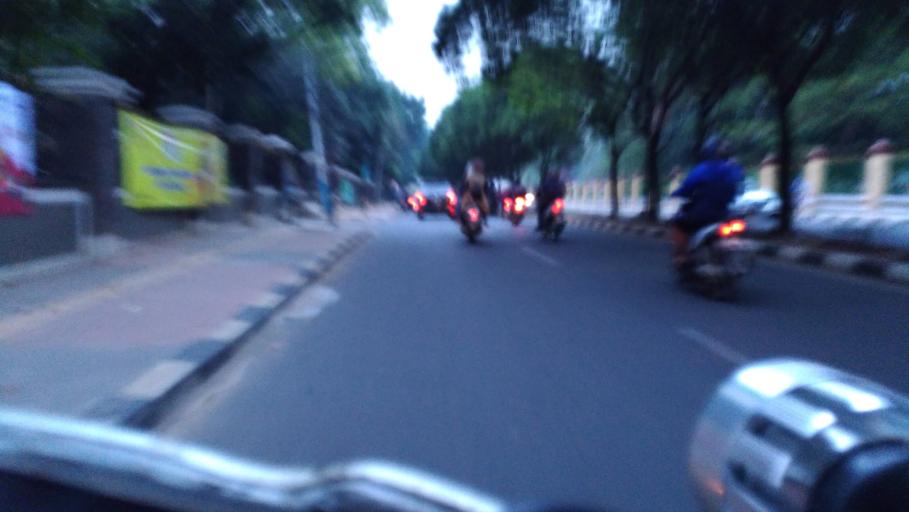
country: ID
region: West Java
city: Cileungsir
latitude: -6.3690
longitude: 106.8909
